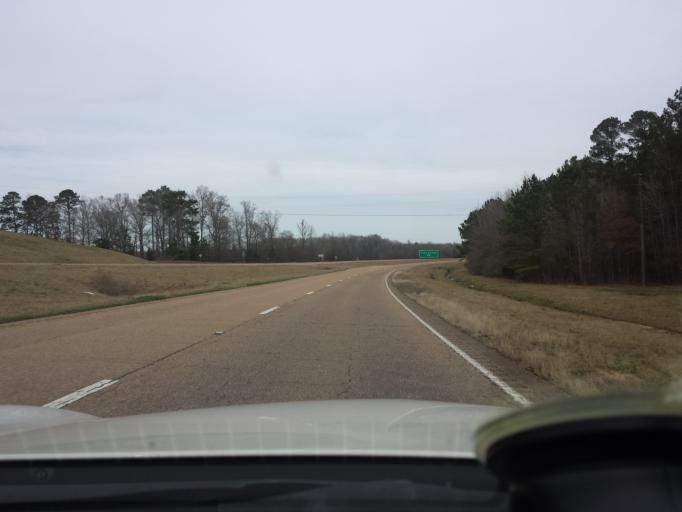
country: US
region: Mississippi
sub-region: Oktibbeha County
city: Starkville
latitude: 33.3122
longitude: -88.9092
